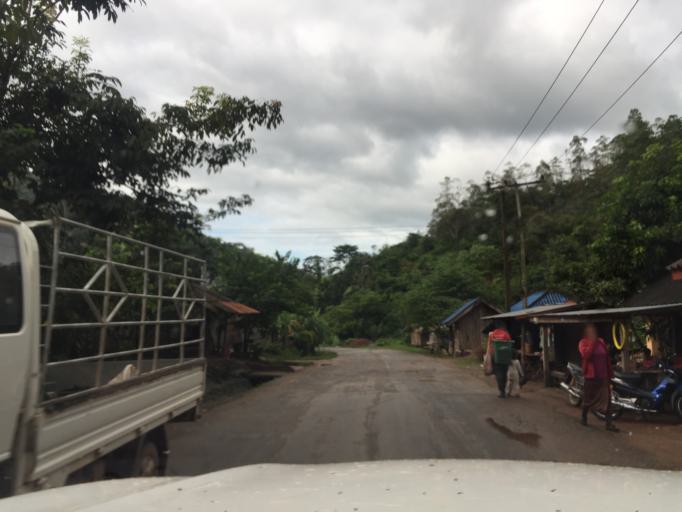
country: LA
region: Oudomxai
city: Muang La
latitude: 20.8144
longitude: 102.0916
